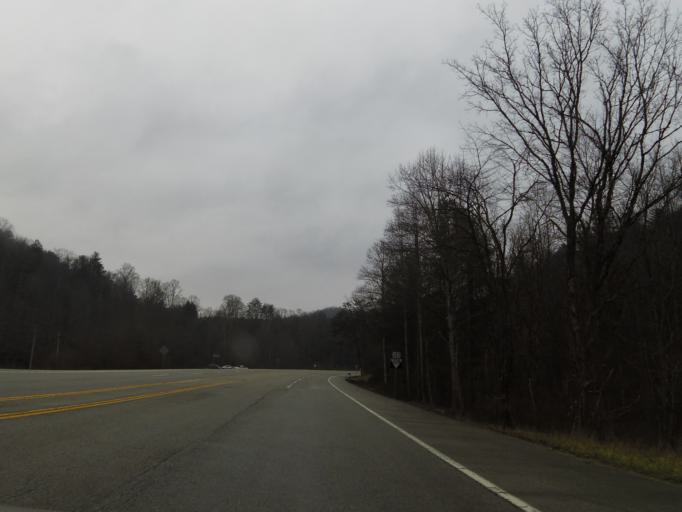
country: US
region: Tennessee
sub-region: Roane County
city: Harriman
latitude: 36.0137
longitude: -84.5241
